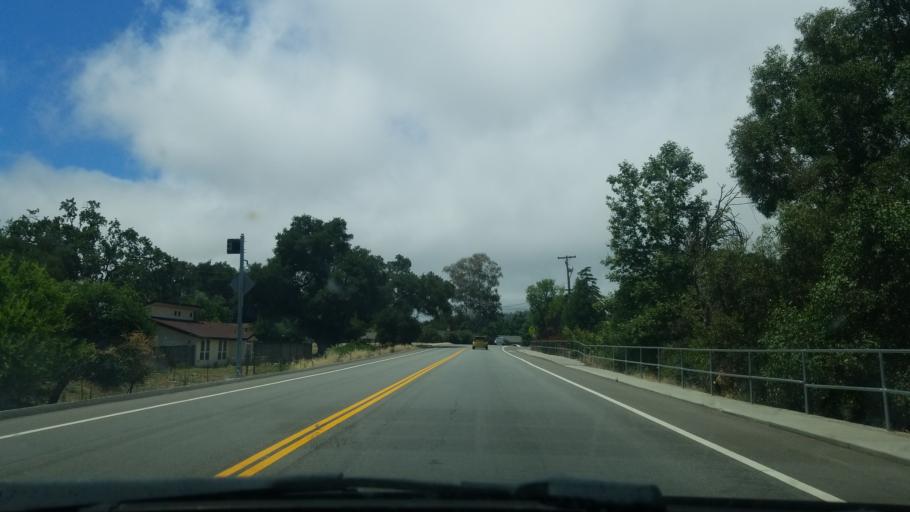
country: US
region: California
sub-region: San Luis Obispo County
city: Atascadero
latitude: 35.4652
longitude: -120.6527
